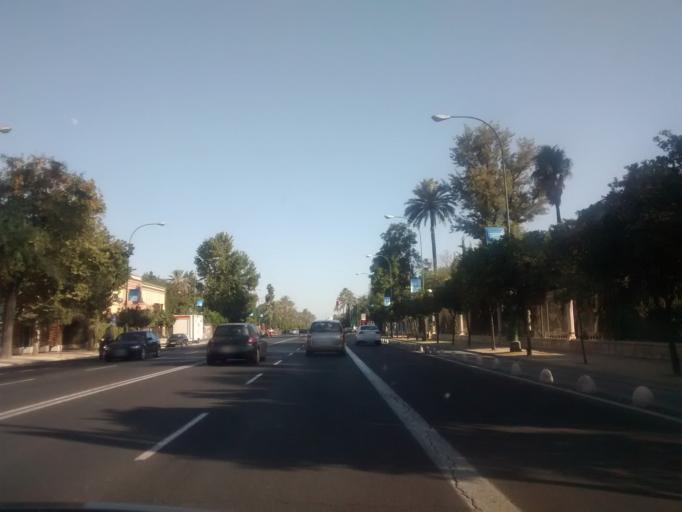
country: ES
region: Andalusia
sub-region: Provincia de Sevilla
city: Sevilla
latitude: 37.3709
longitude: -5.9888
